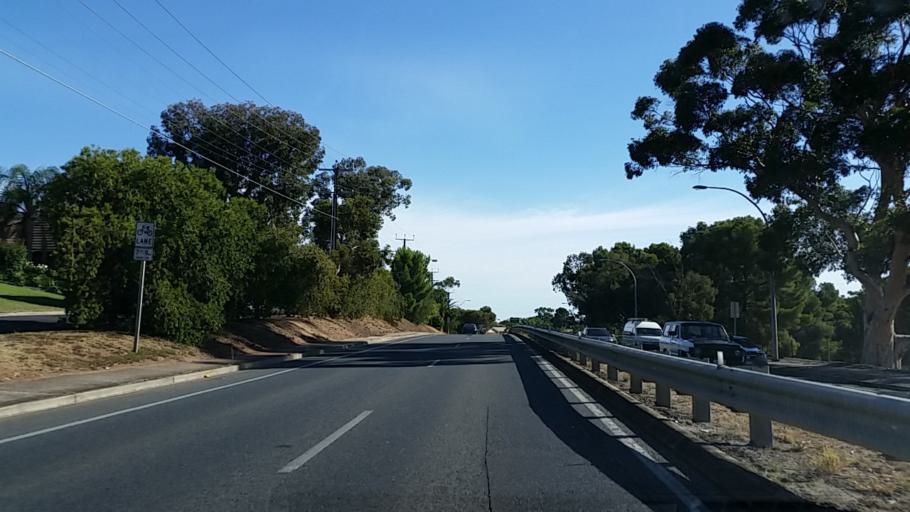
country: AU
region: South Australia
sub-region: Campbelltown
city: Athelstone
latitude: -34.8543
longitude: 138.6972
